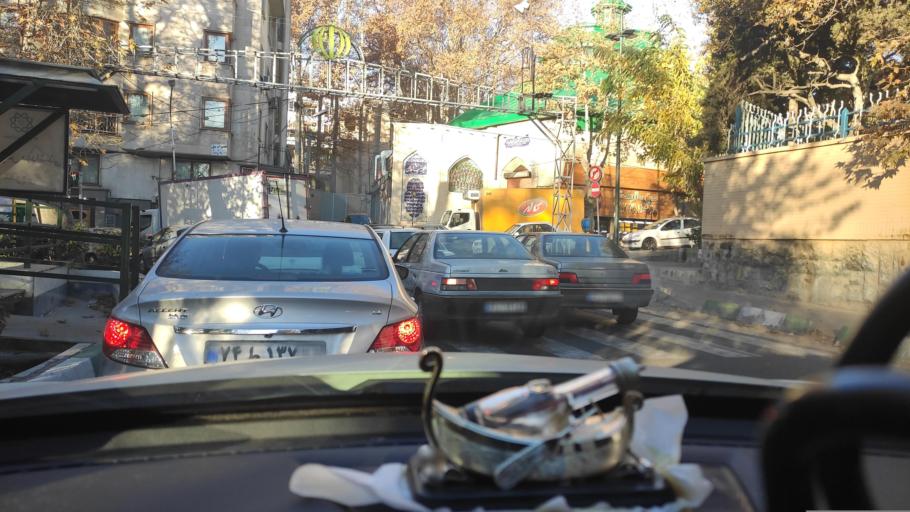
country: IR
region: Tehran
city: Tajrish
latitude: 35.8133
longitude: 51.4711
